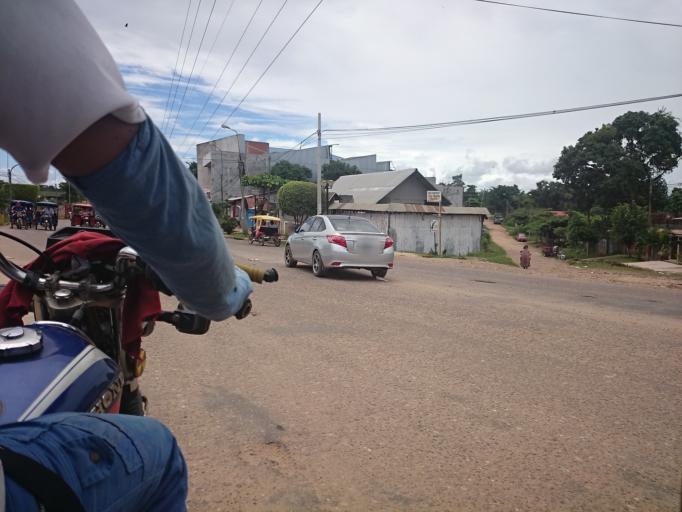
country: PE
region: Ucayali
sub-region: Provincia de Coronel Portillo
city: Pucallpa
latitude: -8.3702
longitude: -74.5598
